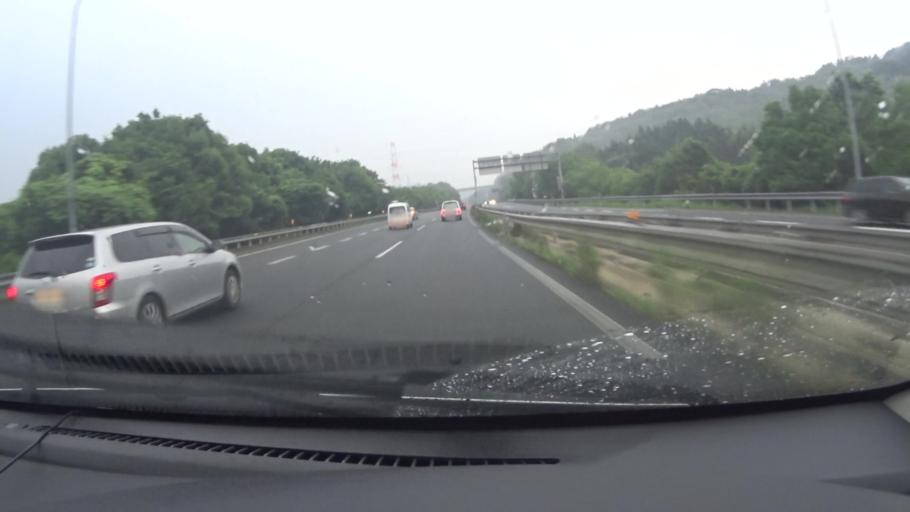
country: JP
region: Kyoto
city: Kameoka
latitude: 34.9907
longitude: 135.6114
